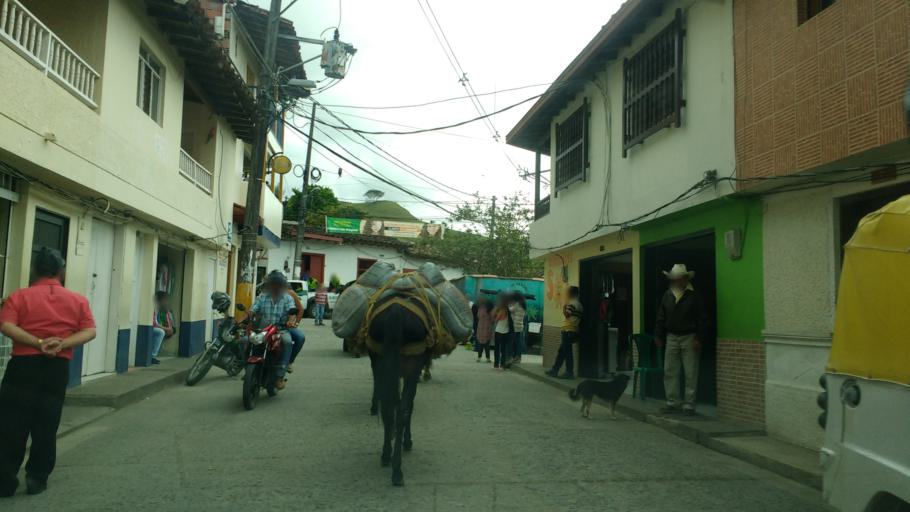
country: CO
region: Antioquia
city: Concepcion
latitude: 6.3945
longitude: -75.2578
